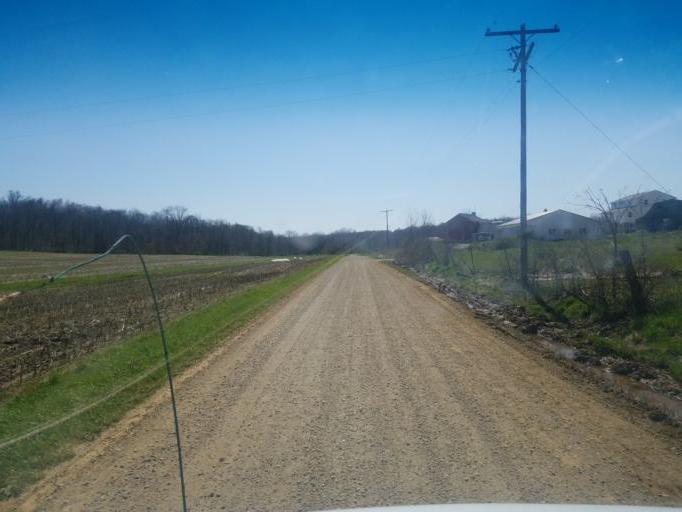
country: US
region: Ohio
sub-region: Knox County
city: Oak Hill
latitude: 40.3287
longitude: -82.1924
